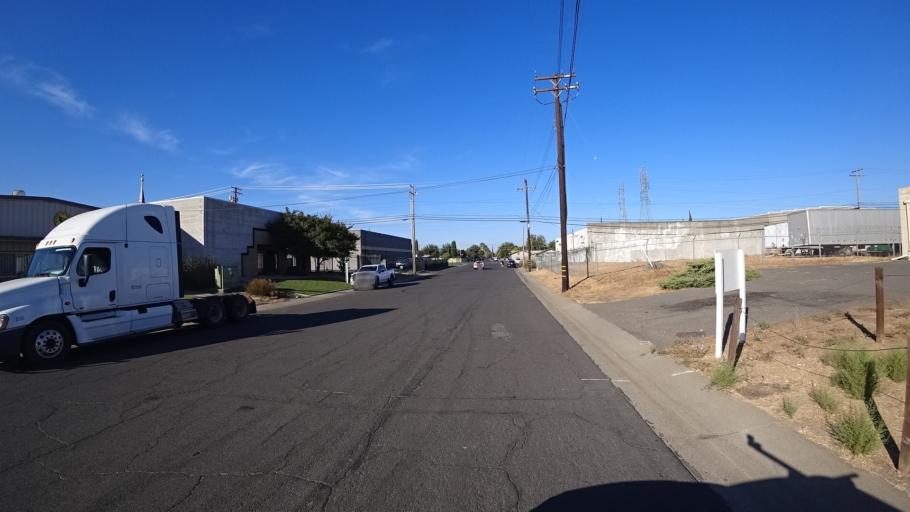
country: US
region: California
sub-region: Sacramento County
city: Florin
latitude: 38.5206
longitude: -121.4077
